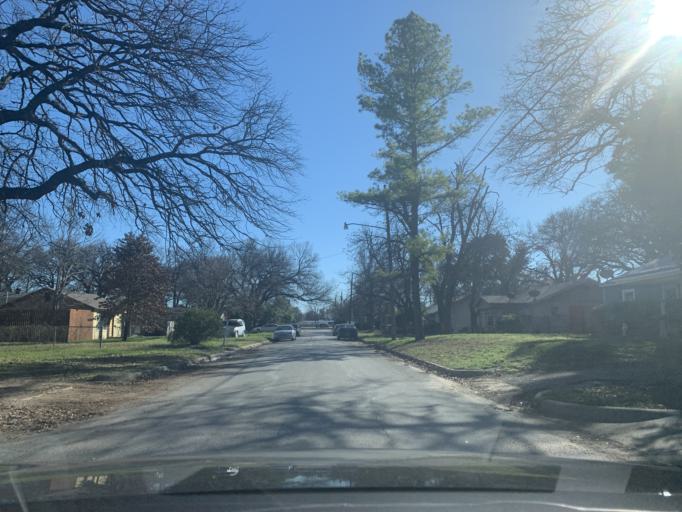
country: US
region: Texas
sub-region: Tarrant County
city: Haltom City
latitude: 32.7786
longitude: -97.2842
